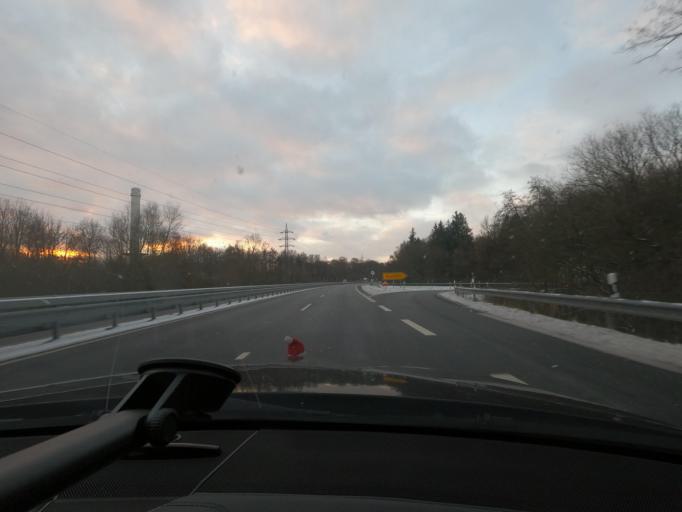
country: DE
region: Schleswig-Holstein
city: Harrislee
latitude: 54.7974
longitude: 9.4094
